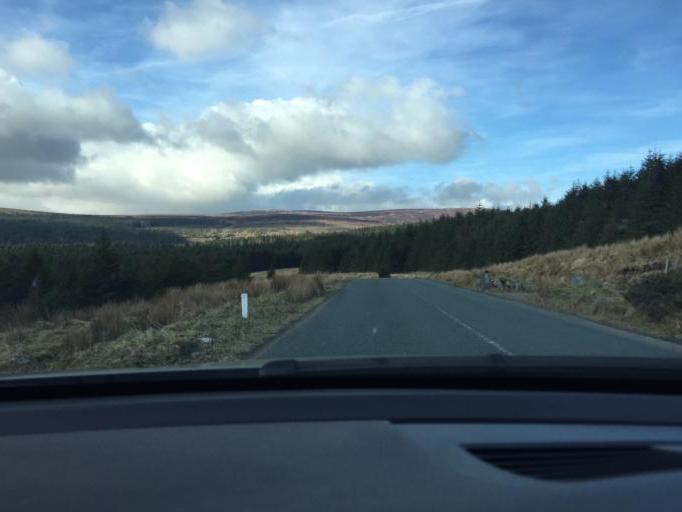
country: IE
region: Leinster
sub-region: Wicklow
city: Valleymount
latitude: 53.0512
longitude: -6.4080
